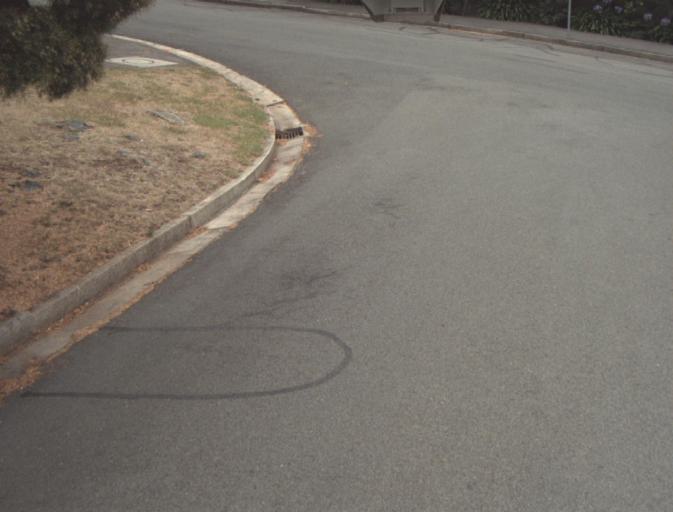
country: AU
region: Tasmania
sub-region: Launceston
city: Launceston
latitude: -41.4404
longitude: 147.1218
